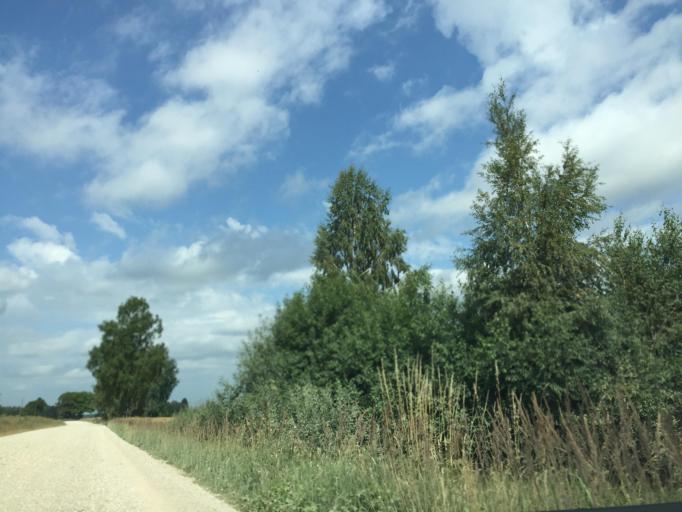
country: LV
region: Kandava
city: Kandava
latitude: 56.9835
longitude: 22.9111
